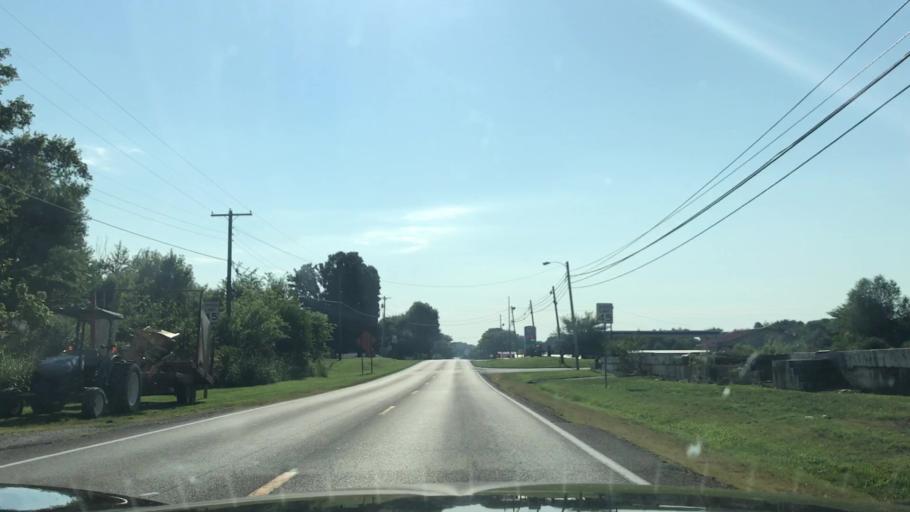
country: US
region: Kentucky
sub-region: Hart County
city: Horse Cave
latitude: 37.1781
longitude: -85.8913
